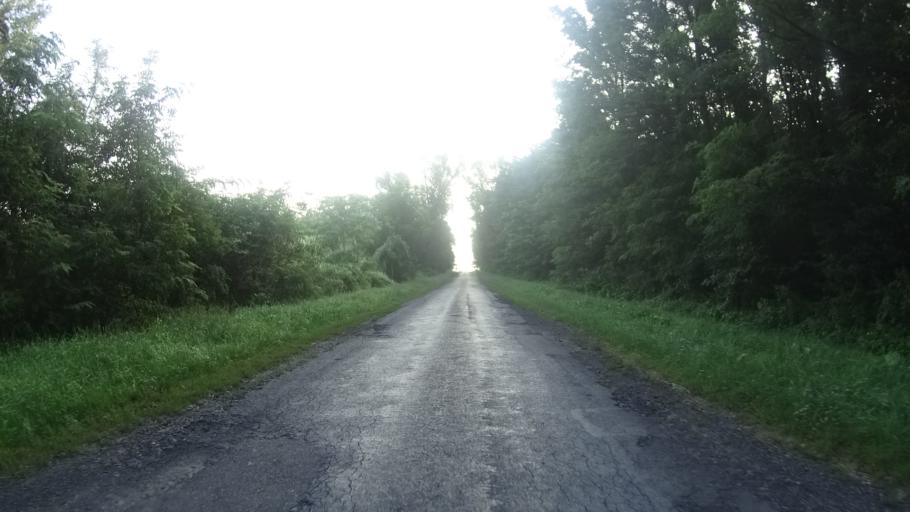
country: HU
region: Zala
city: Zalakomar
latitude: 46.5442
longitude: 17.1598
